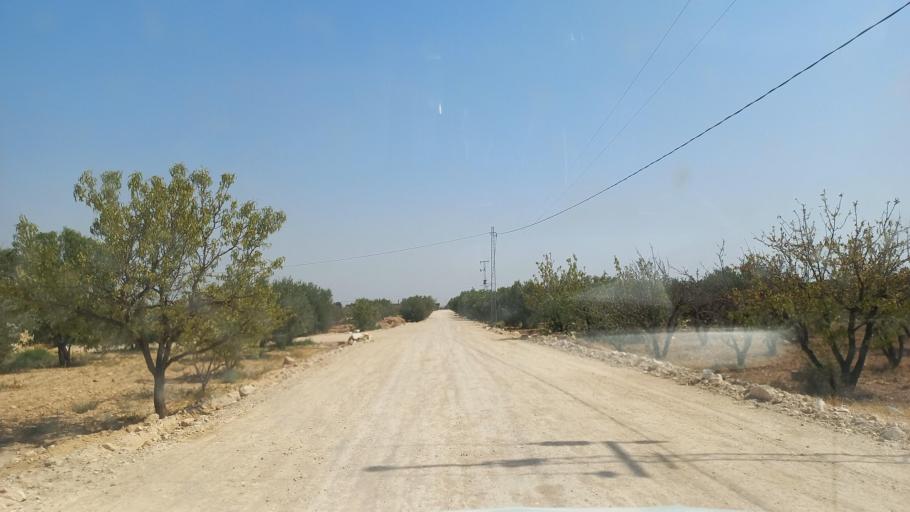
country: TN
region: Al Qasrayn
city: Kasserine
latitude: 35.2588
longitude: 9.0121
